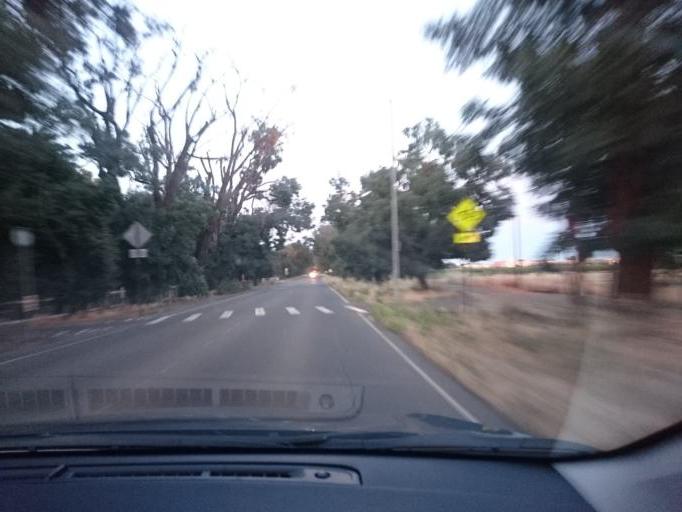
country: US
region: California
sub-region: Yolo County
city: Davis
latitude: 38.5466
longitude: -121.7857
